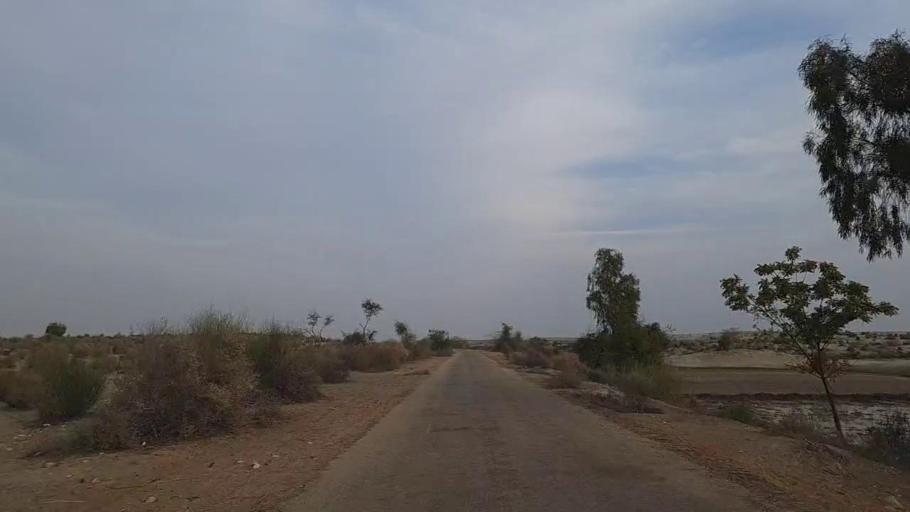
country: PK
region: Sindh
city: Daur
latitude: 26.4942
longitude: 68.5296
